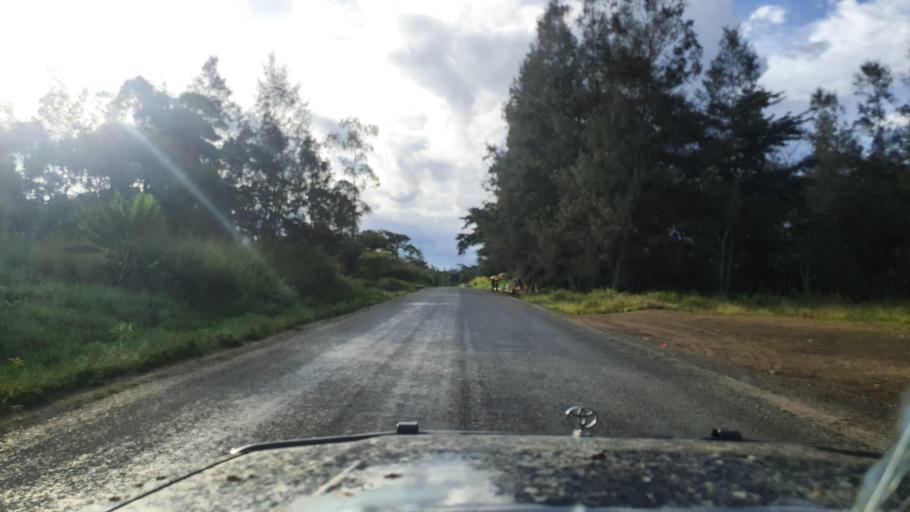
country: PG
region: Jiwaka
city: Minj
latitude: -5.8190
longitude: 144.4939
